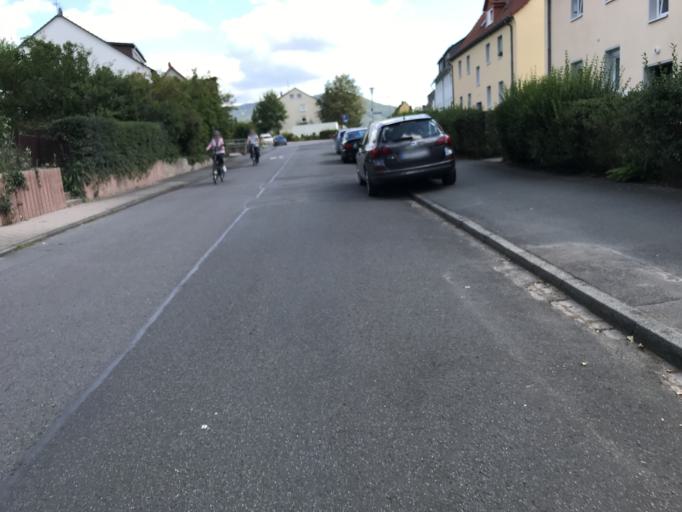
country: DE
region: Hesse
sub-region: Regierungsbezirk Kassel
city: Bad Sooden-Allendorf
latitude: 51.2693
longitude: 9.9826
